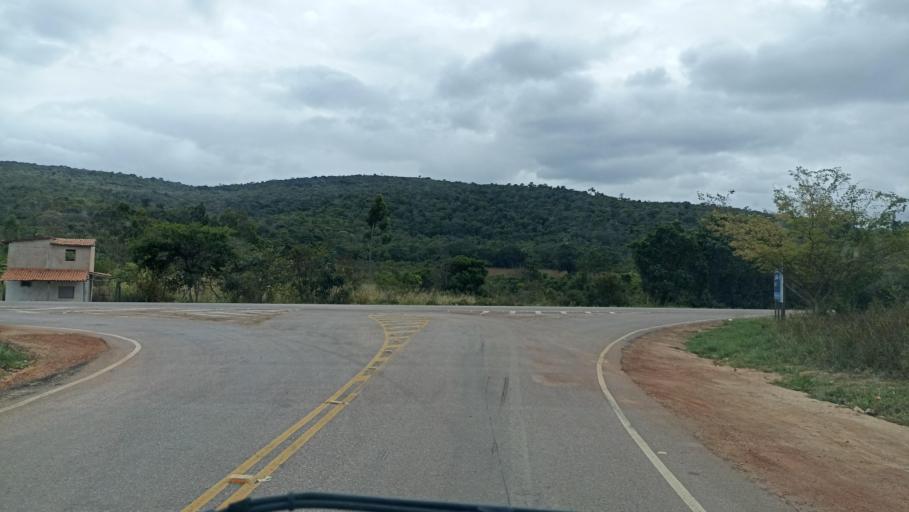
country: BR
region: Bahia
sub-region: Andarai
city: Vera Cruz
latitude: -12.9244
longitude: -41.2331
